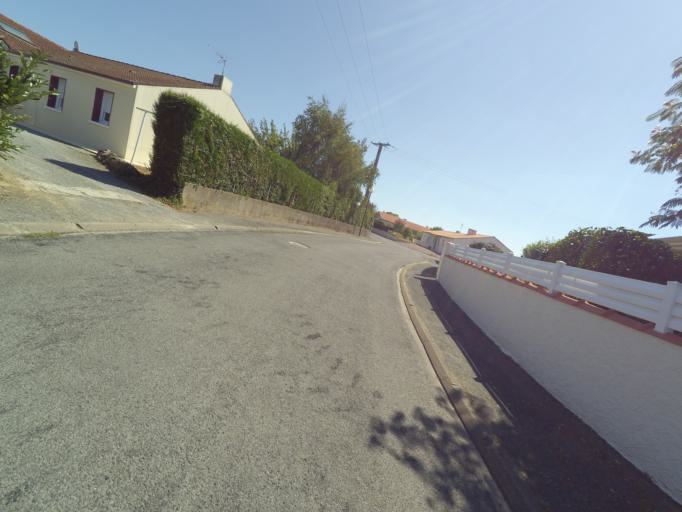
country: FR
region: Pays de la Loire
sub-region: Departement de la Loire-Atlantique
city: Vieillevigne
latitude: 46.9702
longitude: -1.4417
